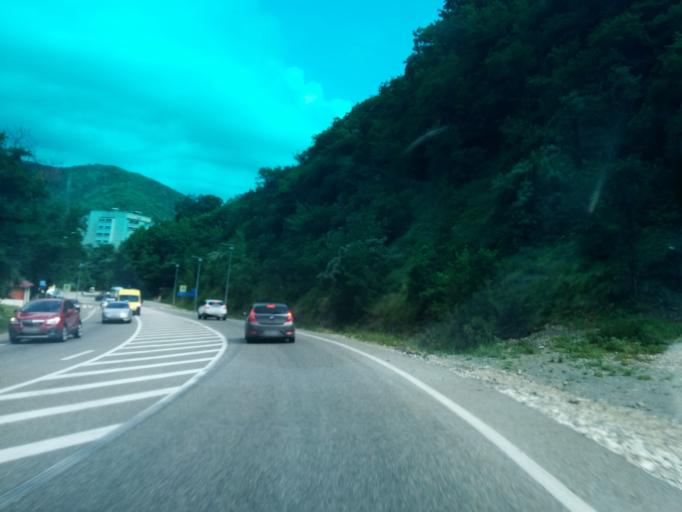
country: RU
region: Krasnodarskiy
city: Nebug
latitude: 44.1759
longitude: 38.9771
